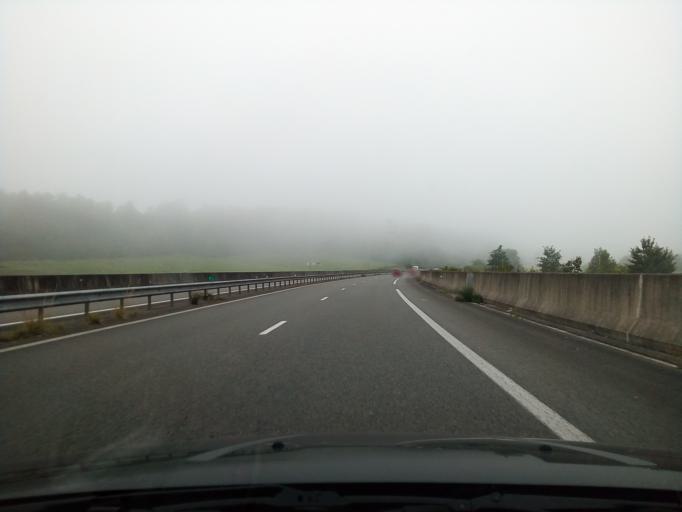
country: FR
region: Poitou-Charentes
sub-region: Departement de la Charente
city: Jarnac
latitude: 45.6665
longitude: -0.1765
